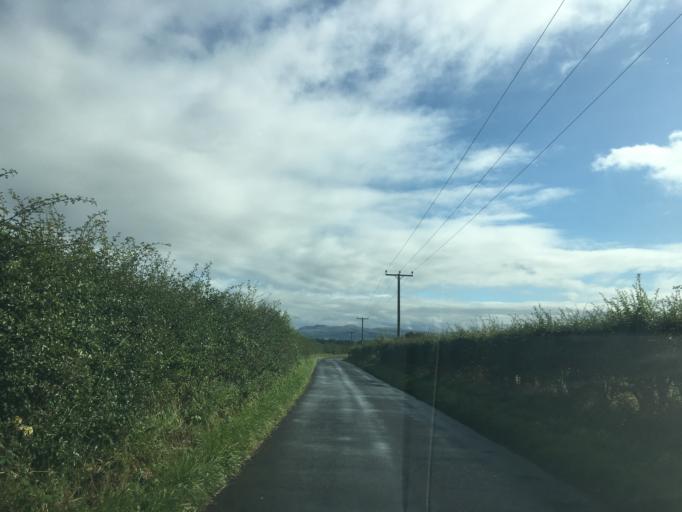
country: GB
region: Scotland
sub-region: Edinburgh
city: Kirkliston
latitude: 55.9632
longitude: -3.3772
